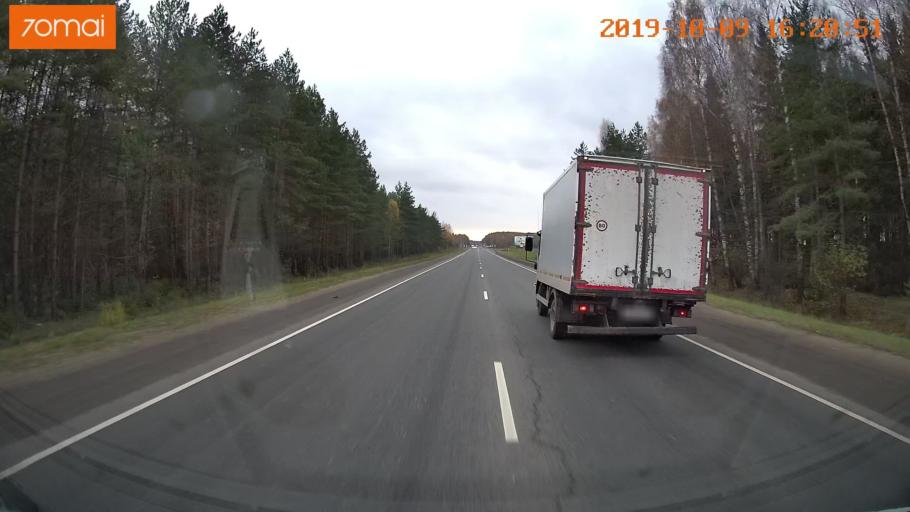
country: RU
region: Kostroma
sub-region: Kostromskoy Rayon
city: Kostroma
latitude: 57.7011
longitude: 40.8911
